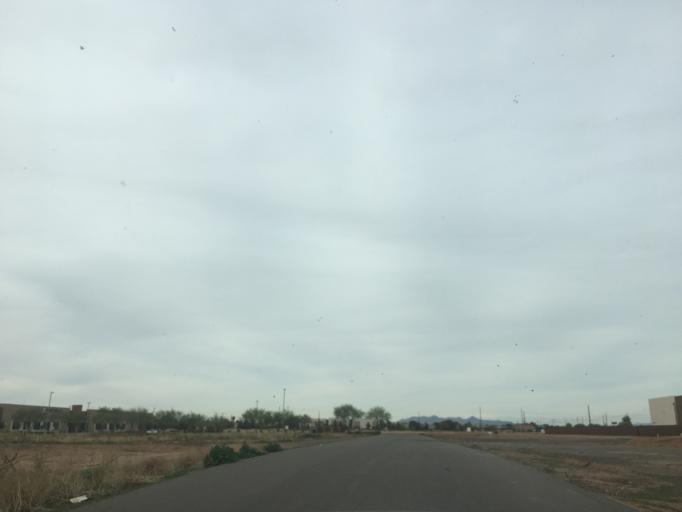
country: US
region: Arizona
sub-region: Maricopa County
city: San Carlos
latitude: 33.3469
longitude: -111.8259
